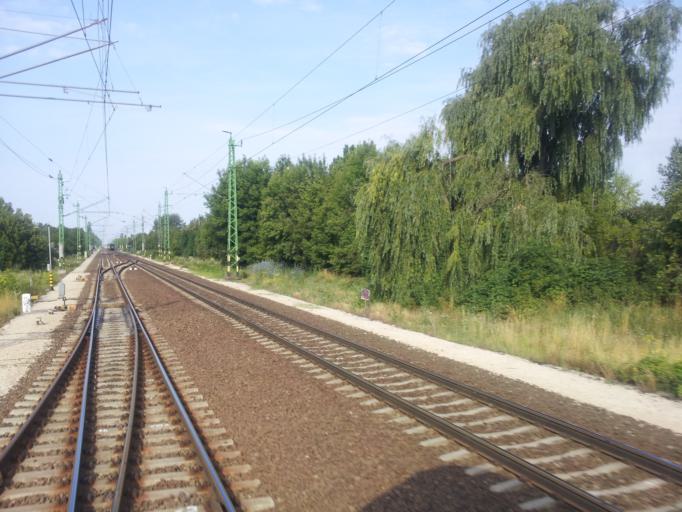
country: HU
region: Fejer
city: Gardony
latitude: 47.2027
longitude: 18.6173
